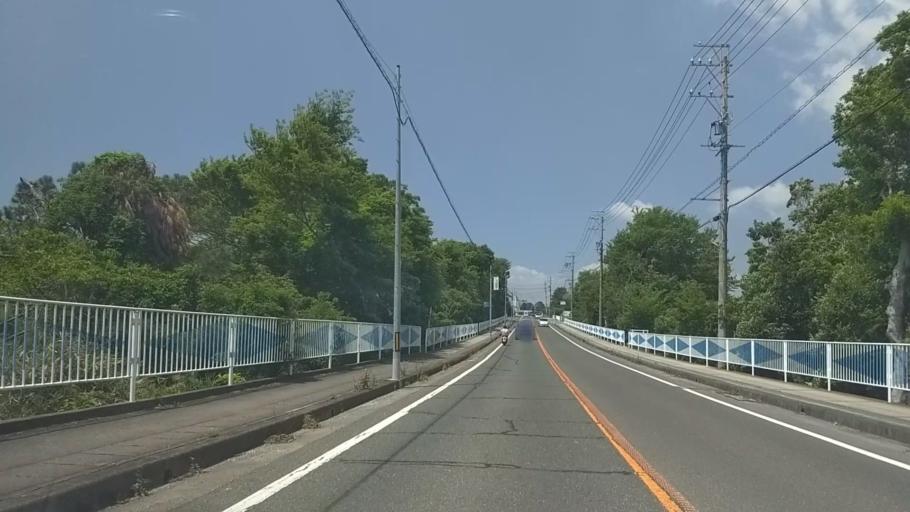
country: JP
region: Shizuoka
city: Hamamatsu
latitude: 34.7403
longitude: 137.7022
